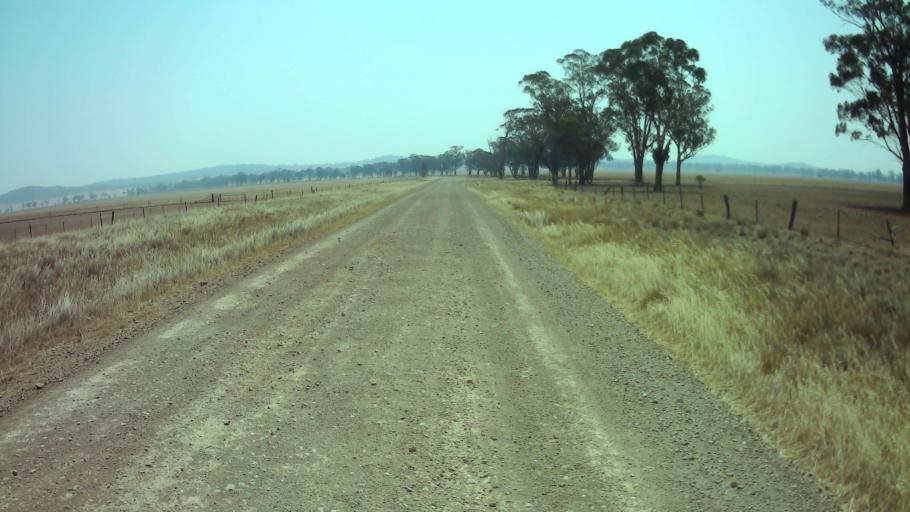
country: AU
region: New South Wales
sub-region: Weddin
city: Grenfell
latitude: -33.6366
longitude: 148.2392
